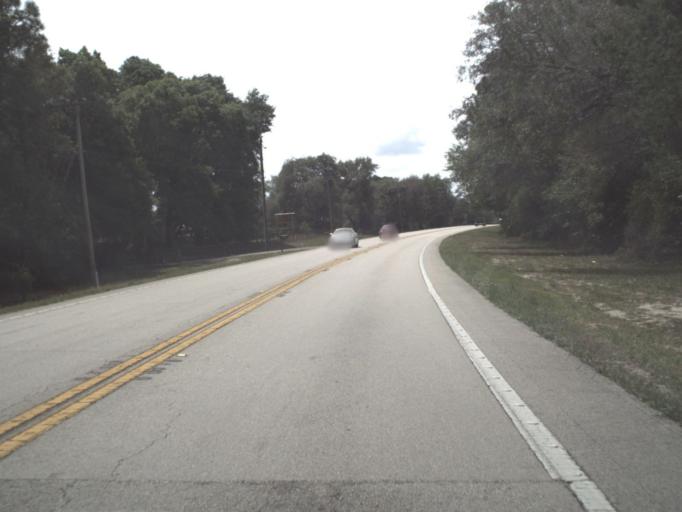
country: US
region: Florida
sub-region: Lake County
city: Lake Mack-Forest Hills
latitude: 28.9008
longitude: -81.4560
